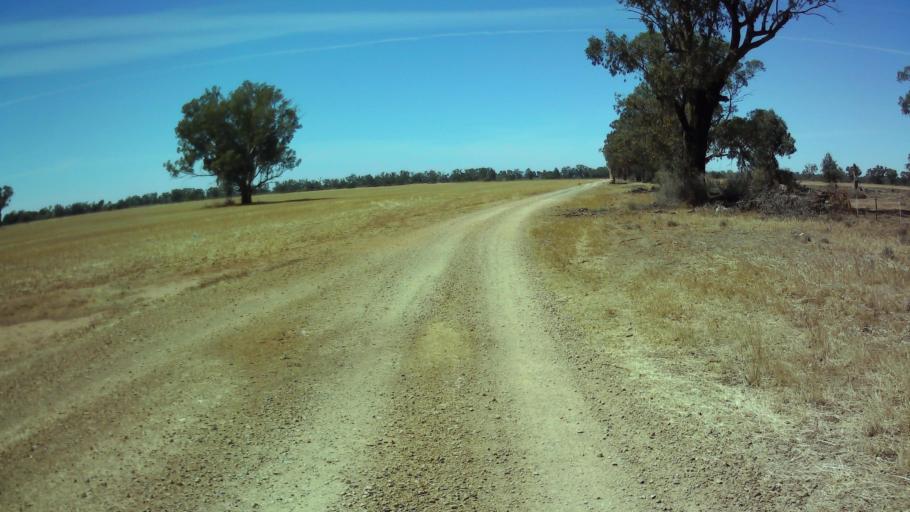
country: AU
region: New South Wales
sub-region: Weddin
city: Grenfell
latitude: -34.0302
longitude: 147.8906
